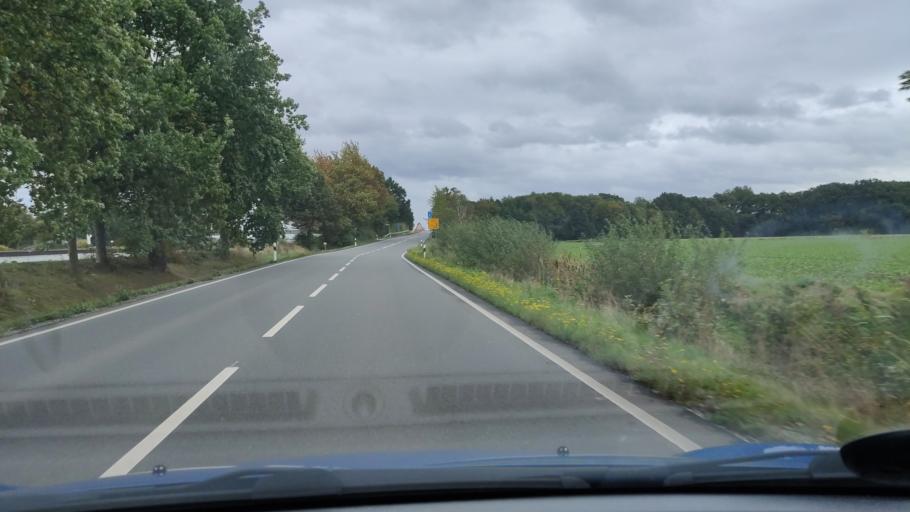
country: DE
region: Lower Saxony
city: Garbsen
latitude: 52.3990
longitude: 9.5452
